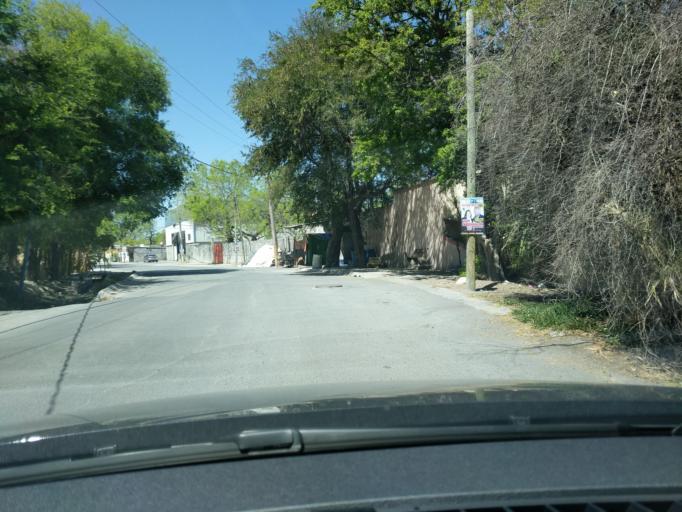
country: MX
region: Nuevo Leon
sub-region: Apodaca
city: Artemio Trevino
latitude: 25.8128
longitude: -100.1335
